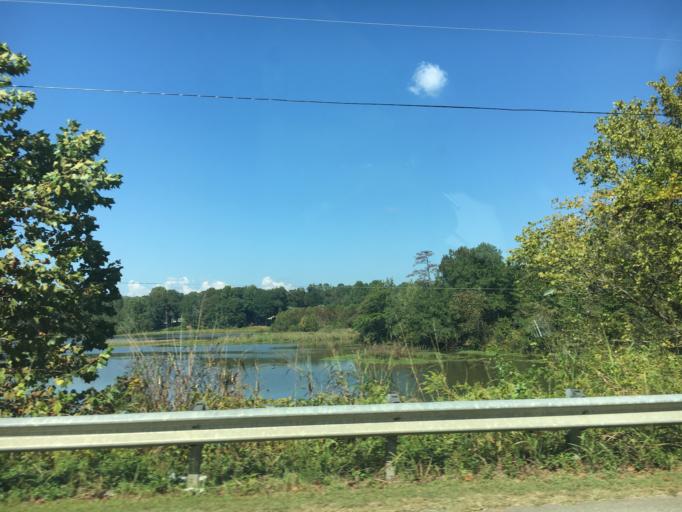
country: US
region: South Carolina
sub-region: Spartanburg County
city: Wellford
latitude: 34.8884
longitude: -82.1032
